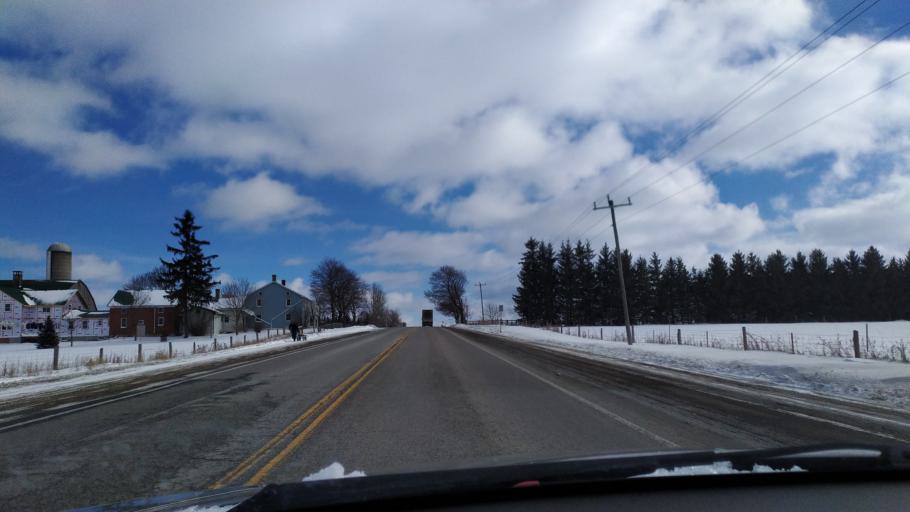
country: CA
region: Ontario
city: Waterloo
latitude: 43.5942
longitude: -80.6209
